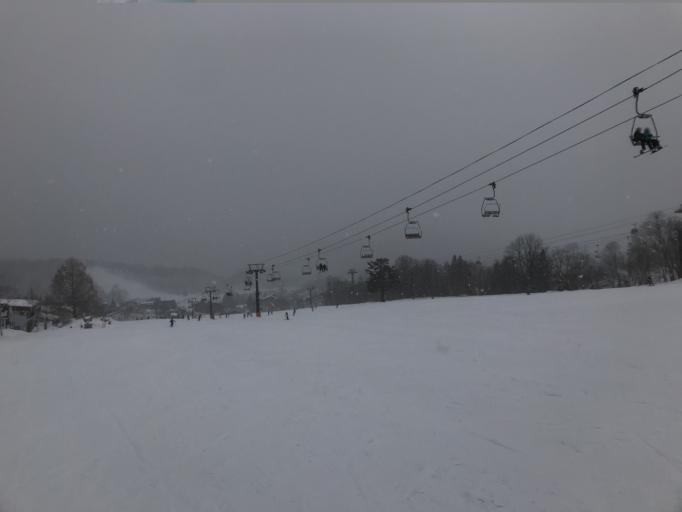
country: JP
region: Nagano
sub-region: Kitaazumi Gun
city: Hakuba
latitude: 36.7533
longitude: 137.8677
